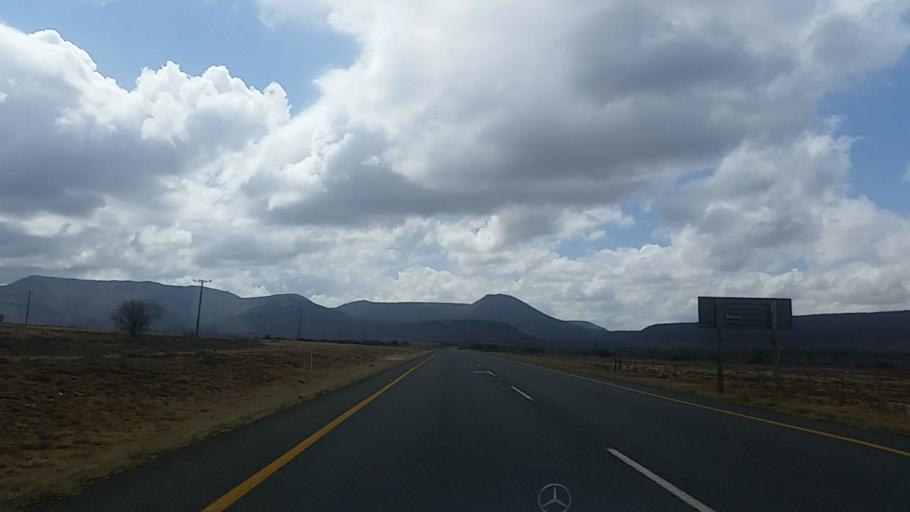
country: ZA
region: Eastern Cape
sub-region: Cacadu District Municipality
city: Graaff-Reinet
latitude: -32.0951
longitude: 24.6043
